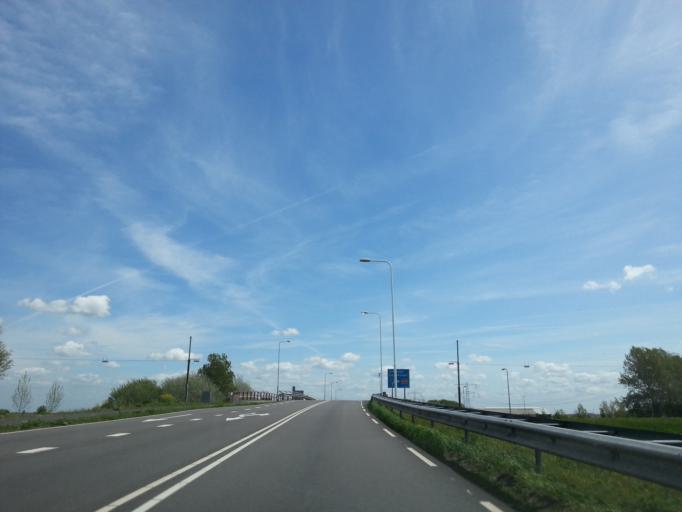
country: NL
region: North Holland
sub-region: Gemeente Beverwijk
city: Beverwijk
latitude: 52.4752
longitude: 4.6824
